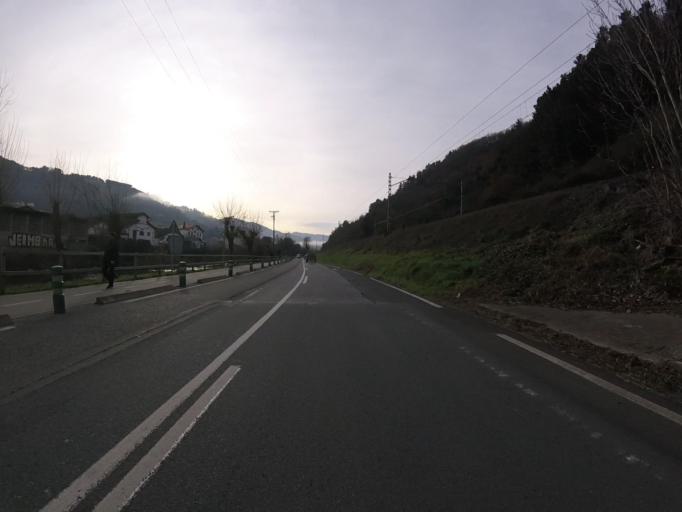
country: ES
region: Basque Country
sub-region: Provincia de Guipuzcoa
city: Anoeta
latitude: 43.1494
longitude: -2.0725
